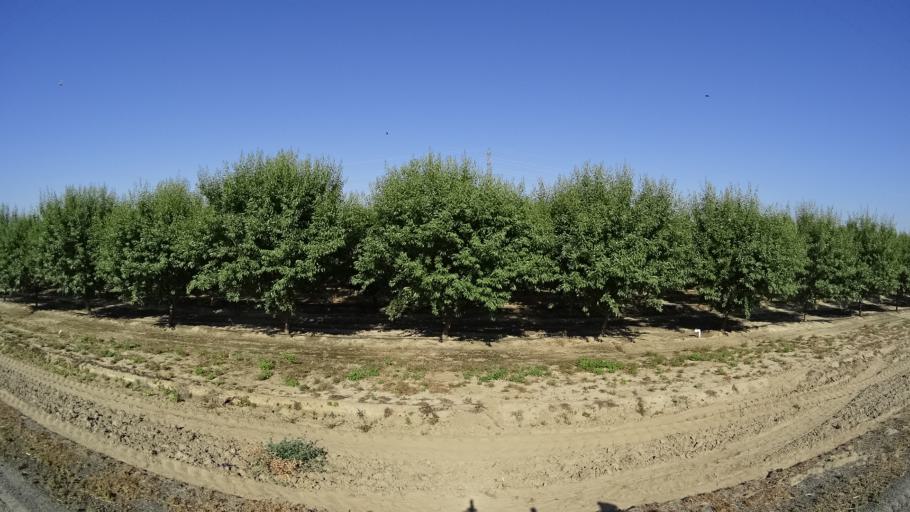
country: US
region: California
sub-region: Fresno County
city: Riverdale
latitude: 36.3663
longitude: -119.8872
